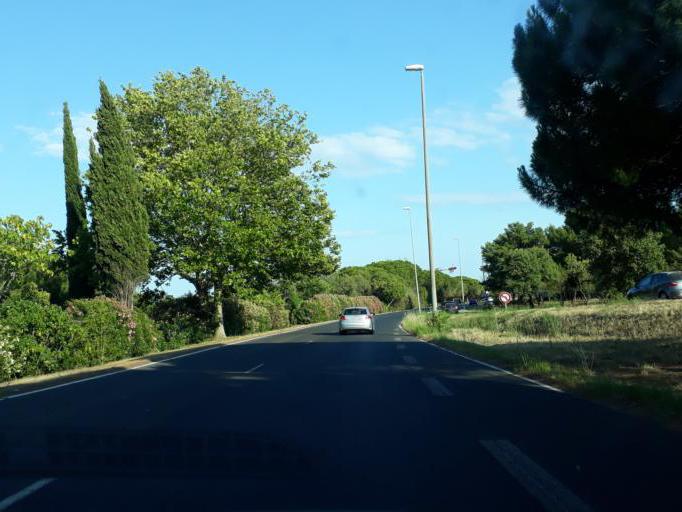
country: FR
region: Languedoc-Roussillon
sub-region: Departement de l'Herault
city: Le Cap d'Agde
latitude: 43.2934
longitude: 3.5044
